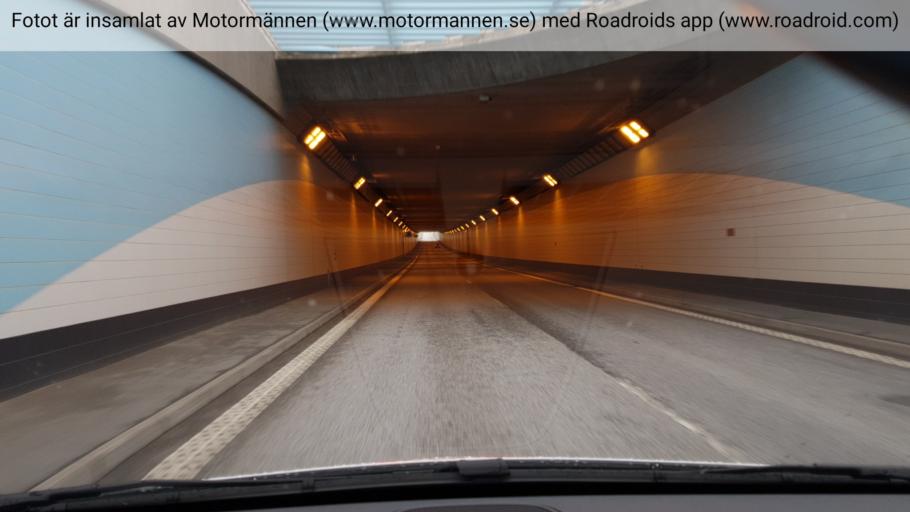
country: SE
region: Vaestra Goetaland
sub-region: Skovde Kommun
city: Skultorp
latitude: 58.3559
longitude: 13.8653
